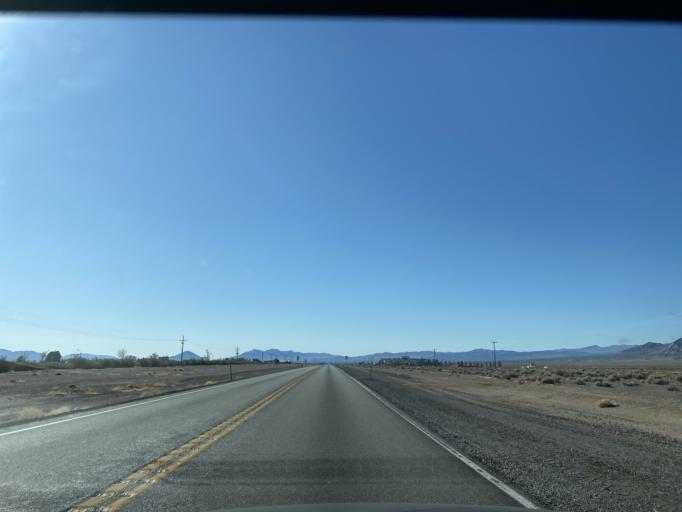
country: US
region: Nevada
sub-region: Nye County
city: Pahrump
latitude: 36.4209
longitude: -116.4222
